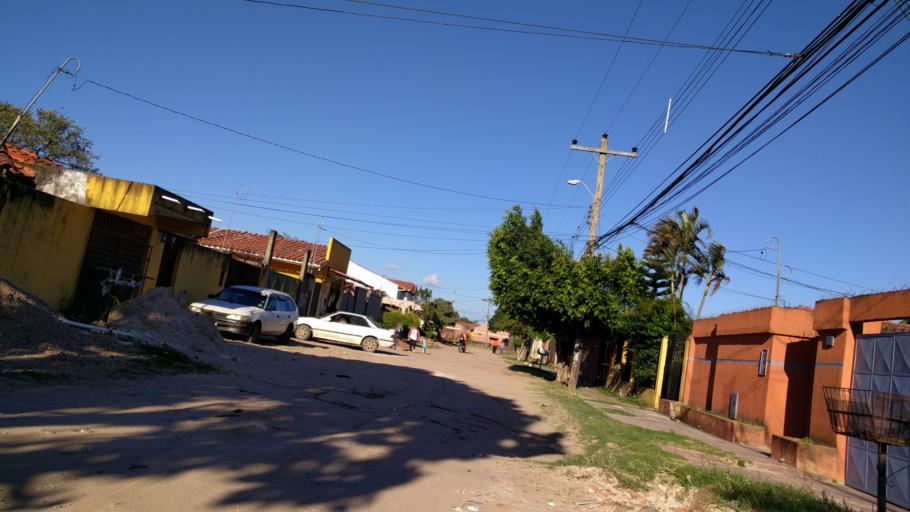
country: BO
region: Santa Cruz
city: Santa Cruz de la Sierra
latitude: -17.8102
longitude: -63.2249
